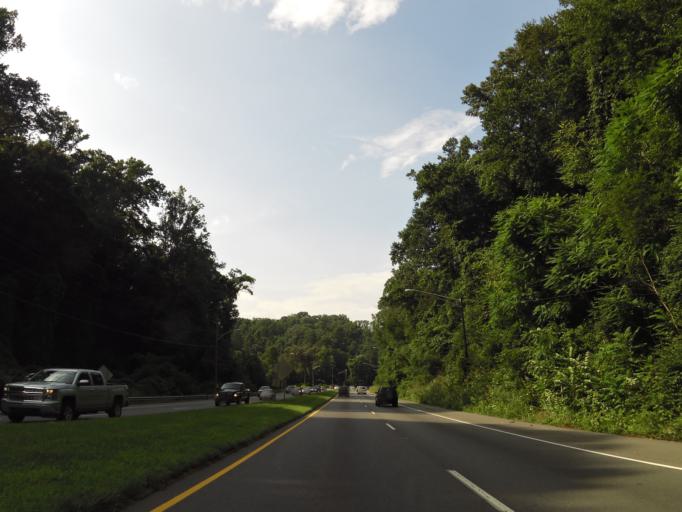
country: US
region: Tennessee
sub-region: Knox County
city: Knoxville
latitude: 35.9181
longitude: -83.9563
